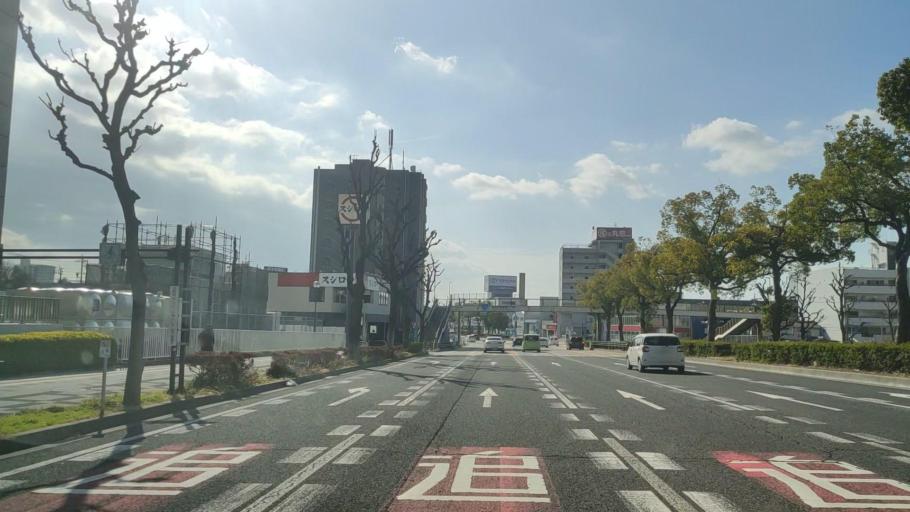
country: JP
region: Aichi
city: Nagoya-shi
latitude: 35.1383
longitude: 136.8998
